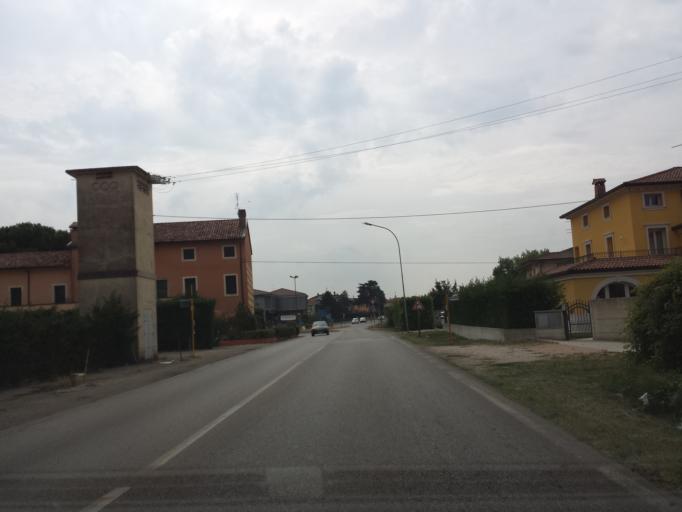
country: IT
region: Veneto
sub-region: Provincia di Verona
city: Brognoligo-Costalunga
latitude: 45.4529
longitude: 11.3027
